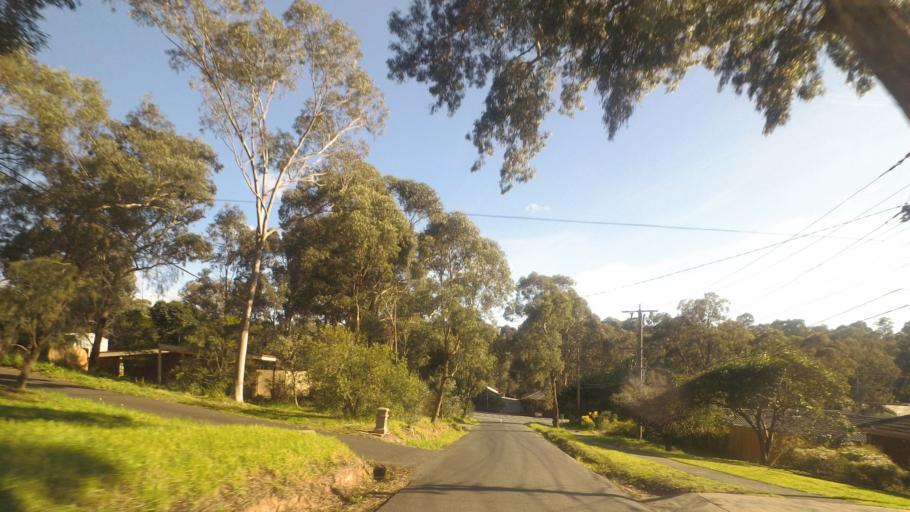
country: AU
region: Victoria
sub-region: Nillumbik
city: Eltham
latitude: -37.7235
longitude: 145.1373
